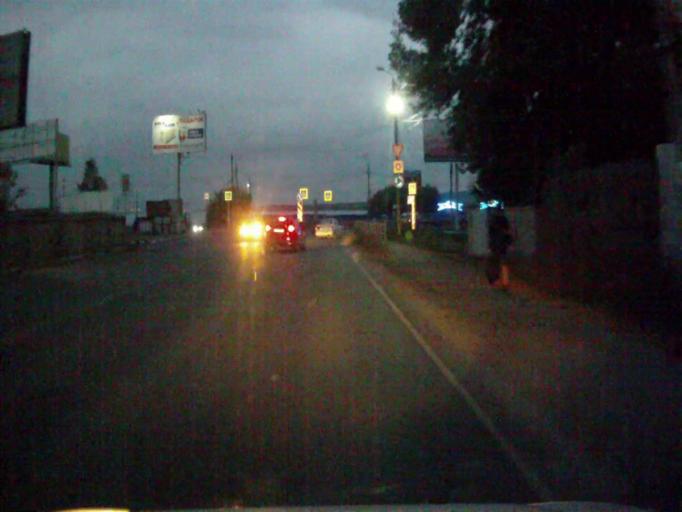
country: RU
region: Chelyabinsk
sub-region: Gorod Chelyabinsk
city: Chelyabinsk
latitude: 55.1493
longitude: 61.3030
